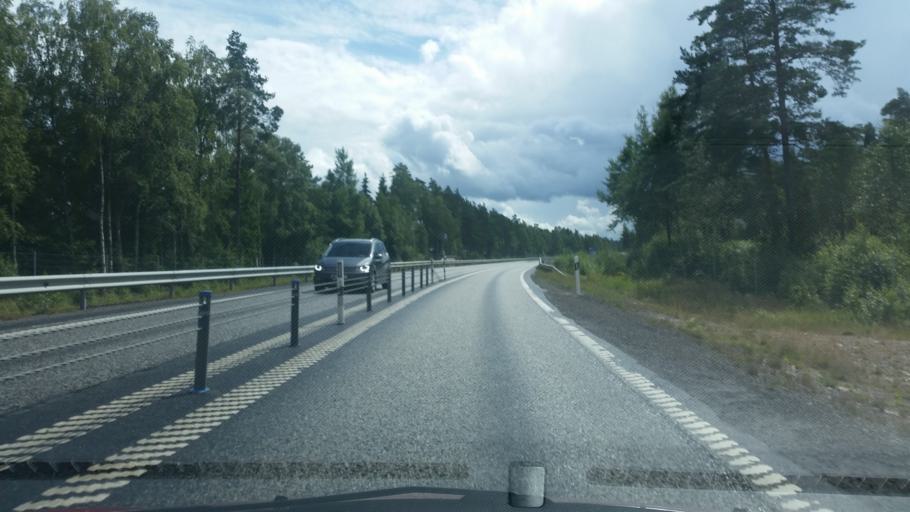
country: SE
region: Joenkoeping
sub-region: Gislaveds Kommun
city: Gislaved
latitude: 57.2804
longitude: 13.6113
